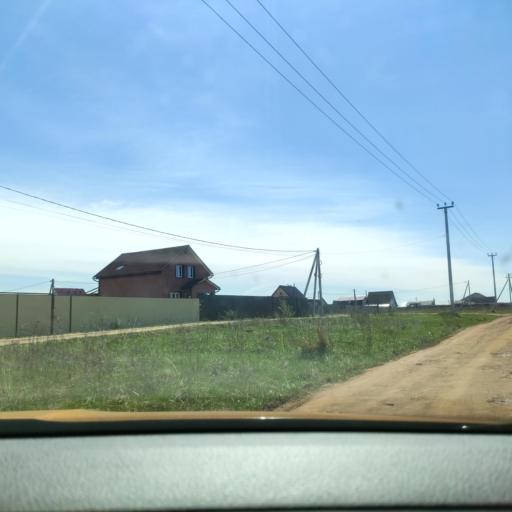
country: RU
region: Moskovskaya
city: Beloozerskiy
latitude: 55.3722
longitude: 38.4047
